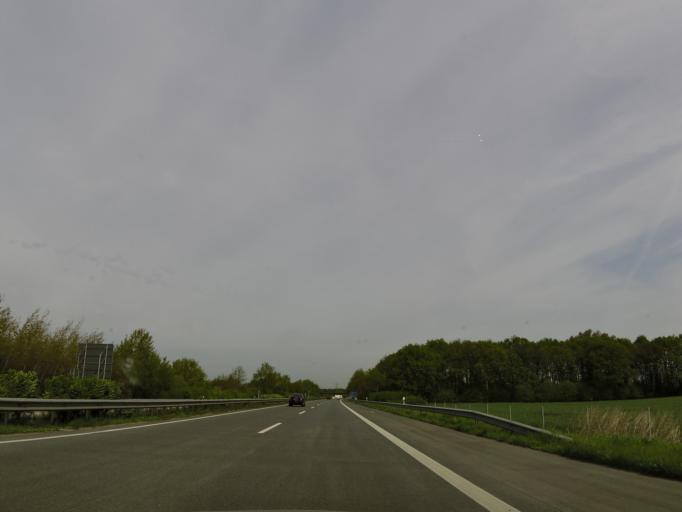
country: DE
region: Schleswig-Holstein
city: Kolln-Reisiek
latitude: 53.7512
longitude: 9.7101
